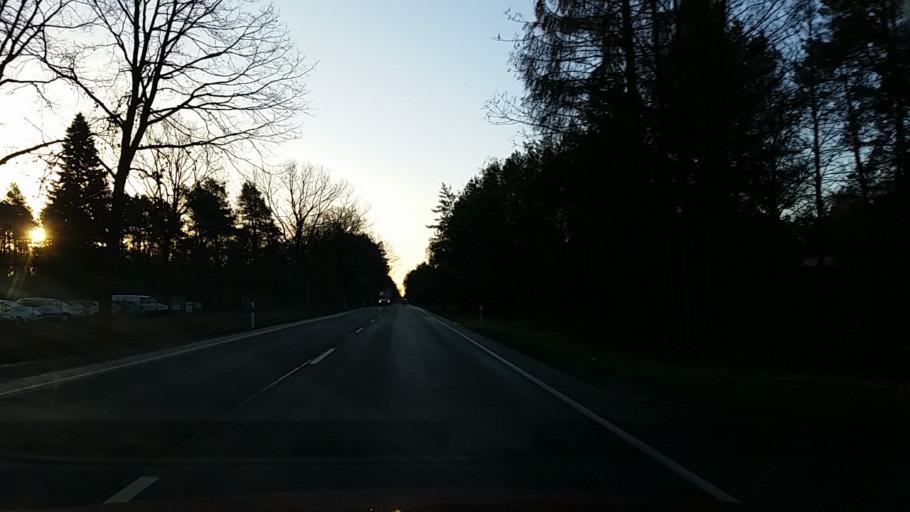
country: DE
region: Lower Saxony
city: Wagenhoff
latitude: 52.5618
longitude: 10.5082
